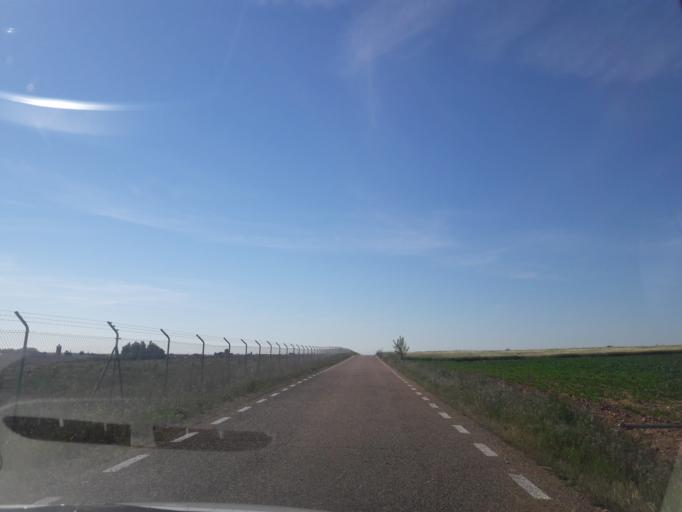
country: ES
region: Castille and Leon
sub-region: Provincia de Salamanca
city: Parada de Rubiales
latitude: 41.1537
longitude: -5.4467
